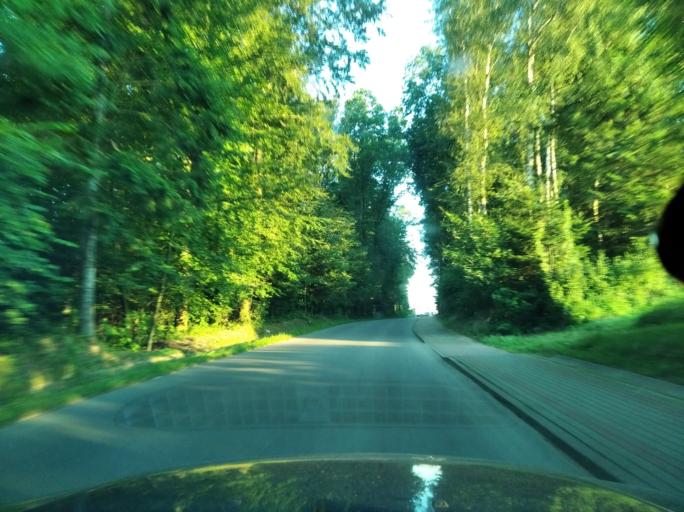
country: PL
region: Subcarpathian Voivodeship
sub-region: Powiat krosnienski
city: Kroscienko Wyzne
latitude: 49.6683
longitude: 21.8305
